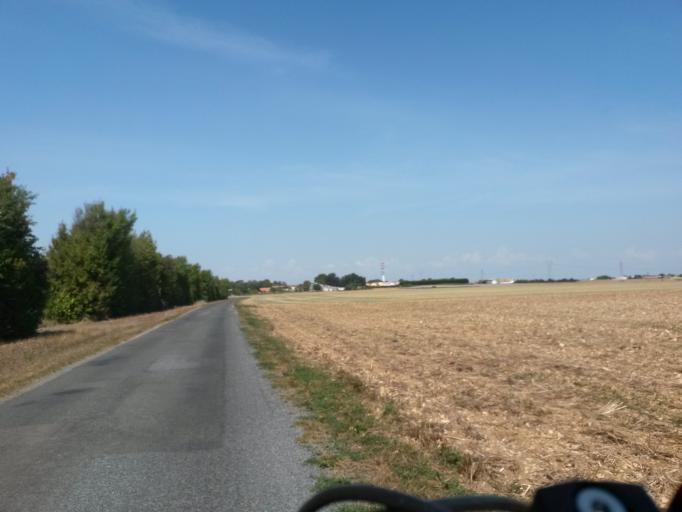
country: FR
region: Poitou-Charentes
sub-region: Departement de la Charente-Maritime
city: Puilboreau
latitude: 46.1950
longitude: -1.1289
